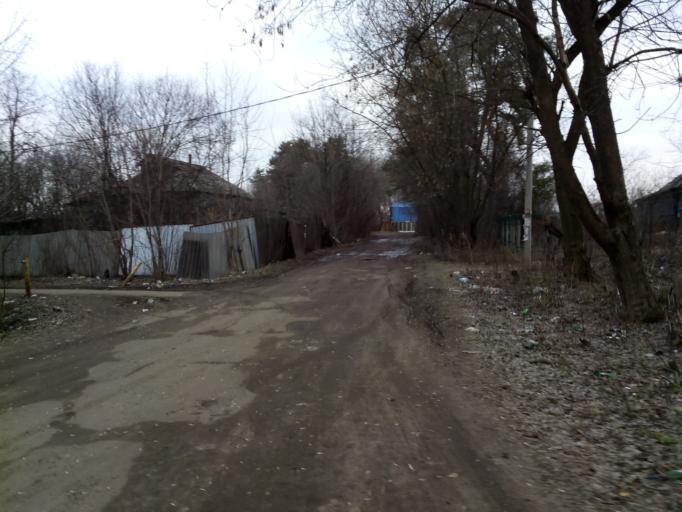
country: RU
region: Moskovskaya
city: Orud'yevo
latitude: 56.4454
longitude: 37.5206
